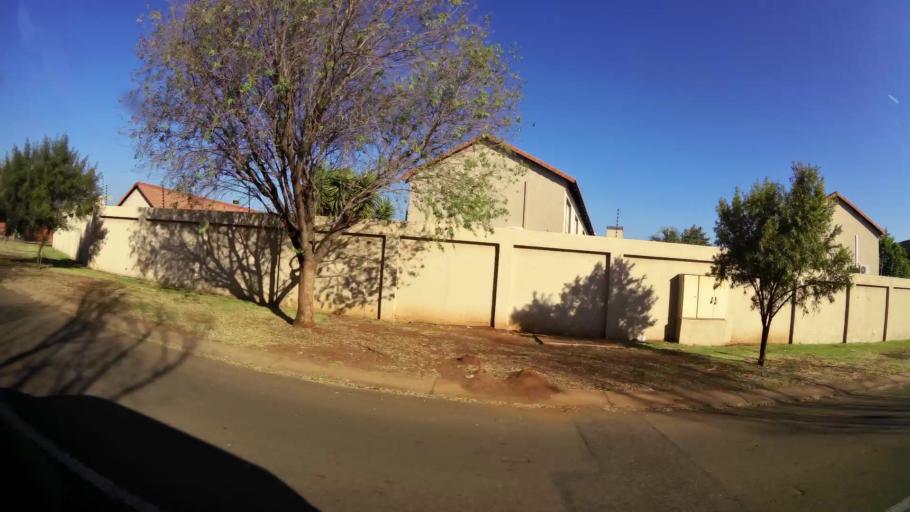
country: ZA
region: Gauteng
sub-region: City of Tshwane Metropolitan Municipality
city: Pretoria
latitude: -25.6679
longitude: 28.1964
